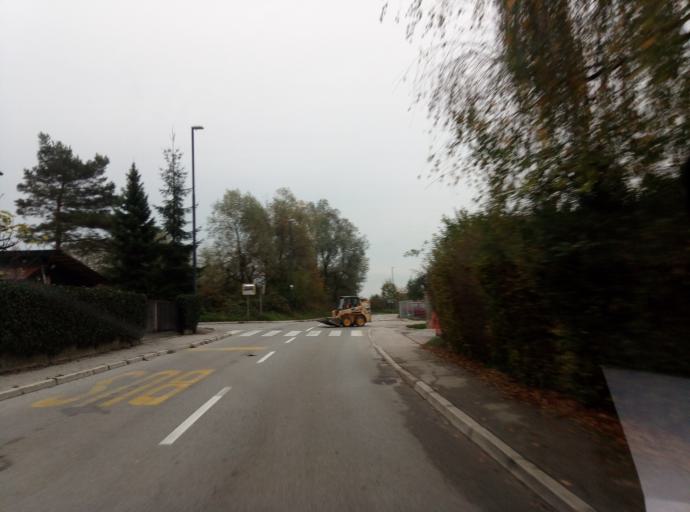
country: SI
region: Trzin
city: Trzin
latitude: 46.1084
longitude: 14.5321
